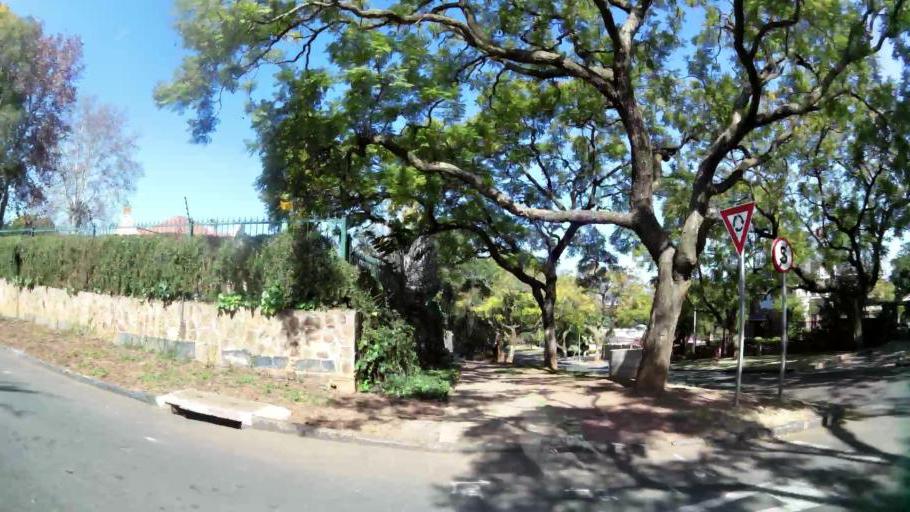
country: ZA
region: Gauteng
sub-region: City of Tshwane Metropolitan Municipality
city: Pretoria
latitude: -25.7419
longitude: 28.2172
